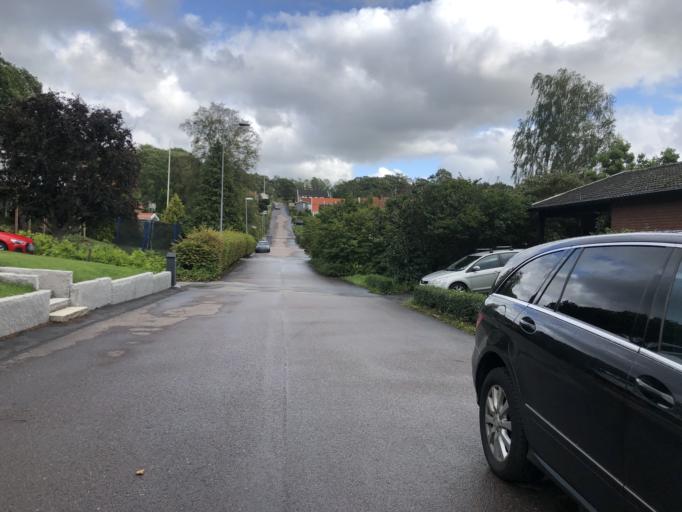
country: SE
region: Vaestra Goetaland
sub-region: Goteborg
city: Goeteborg
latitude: 57.7559
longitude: 11.9331
